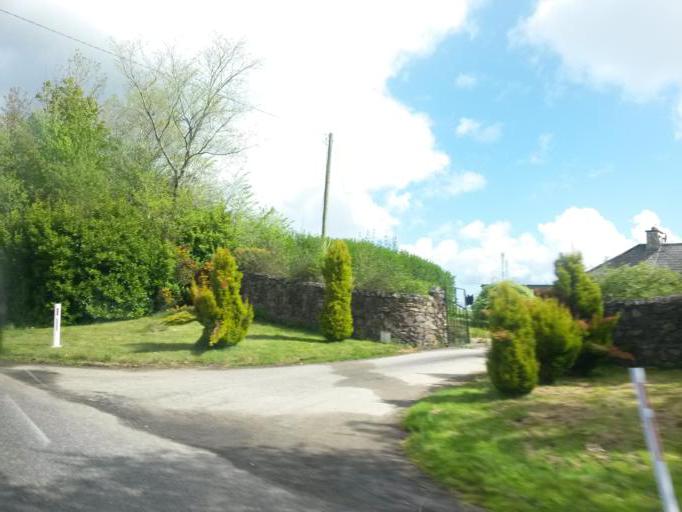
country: IE
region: Leinster
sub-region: Loch Garman
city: Castlebridge
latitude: 52.3701
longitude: -6.5168
